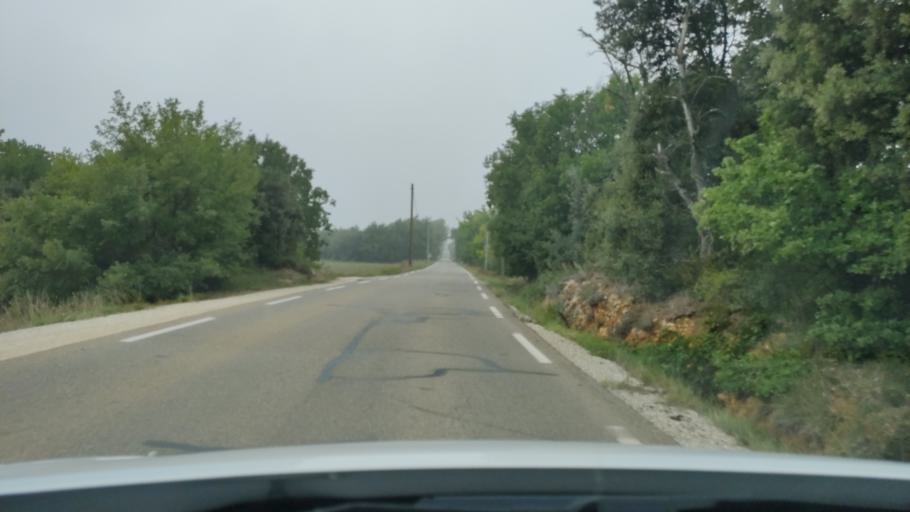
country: FR
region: Provence-Alpes-Cote d'Azur
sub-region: Departement du Vaucluse
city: Bonnieux
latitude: 43.8530
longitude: 5.3094
